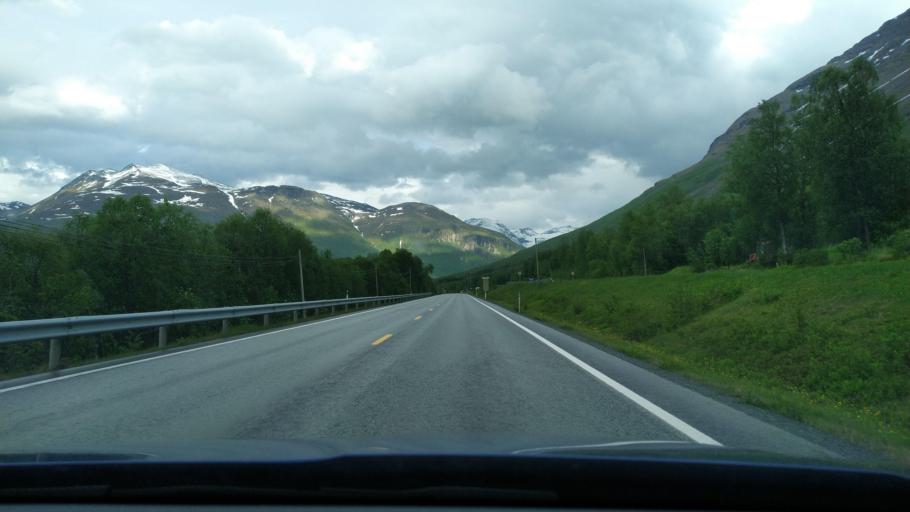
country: NO
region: Troms
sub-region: Balsfjord
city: Storsteinnes
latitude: 69.2139
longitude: 19.5197
